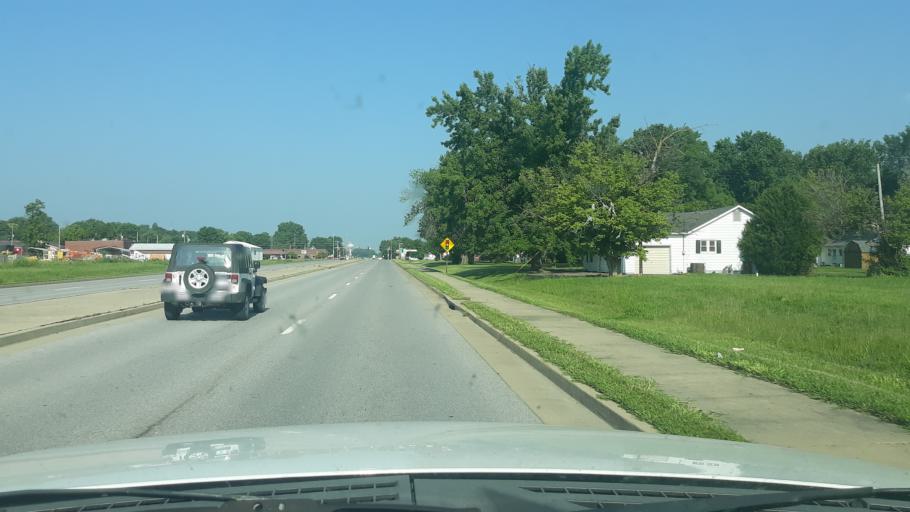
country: US
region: Illinois
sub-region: Saline County
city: Harrisburg
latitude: 37.7434
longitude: -88.5357
